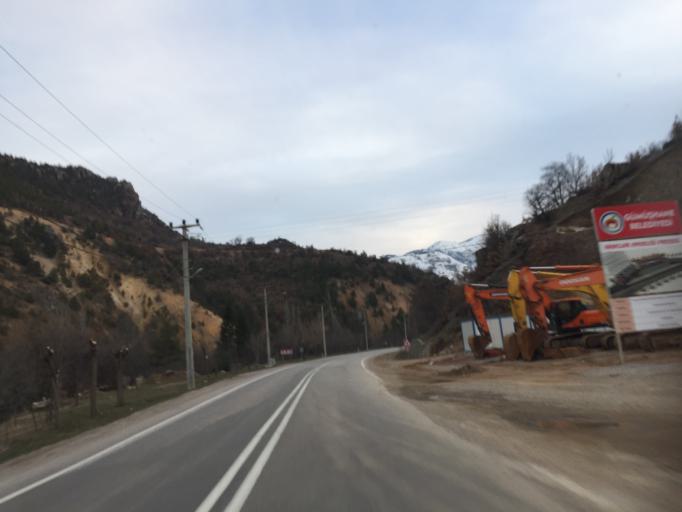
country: TR
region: Gumushane
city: Gumushkhane
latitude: 40.4816
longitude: 39.4623
